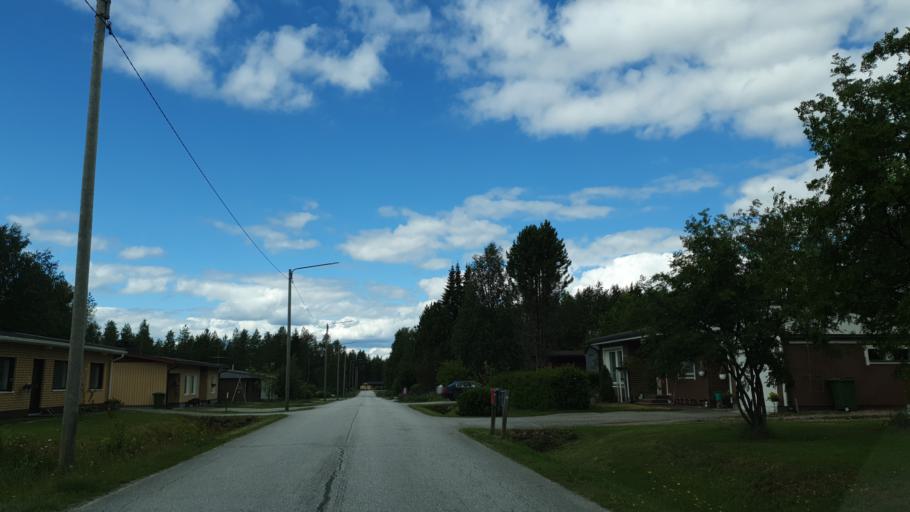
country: FI
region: Kainuu
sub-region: Kehys-Kainuu
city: Kuhmo
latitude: 64.1127
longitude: 29.4861
